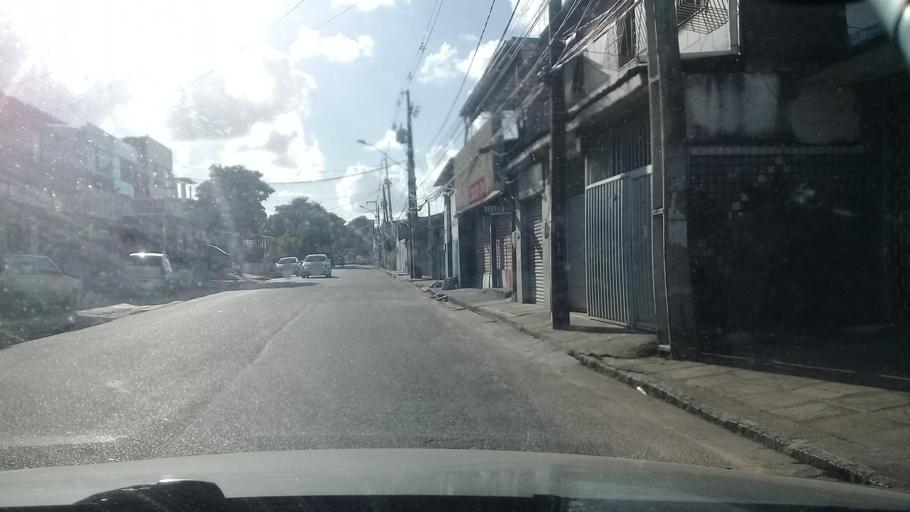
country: BR
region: Pernambuco
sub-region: Jaboatao Dos Guararapes
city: Jaboatao dos Guararapes
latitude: -8.1207
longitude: -34.9377
